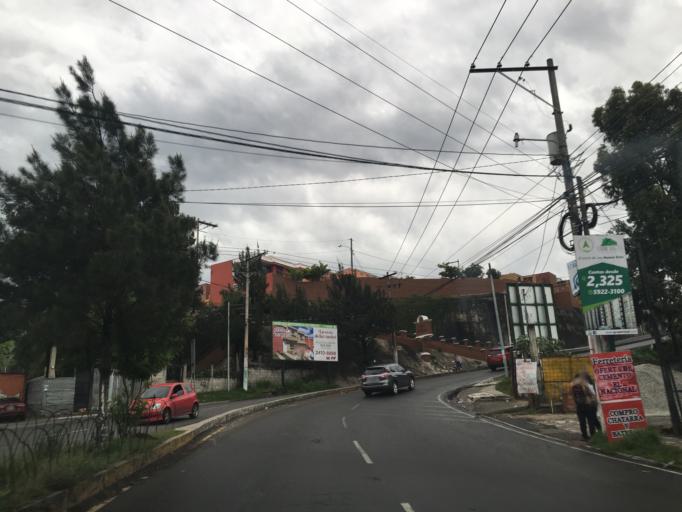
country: GT
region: Guatemala
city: Petapa
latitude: 14.5227
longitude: -90.5490
